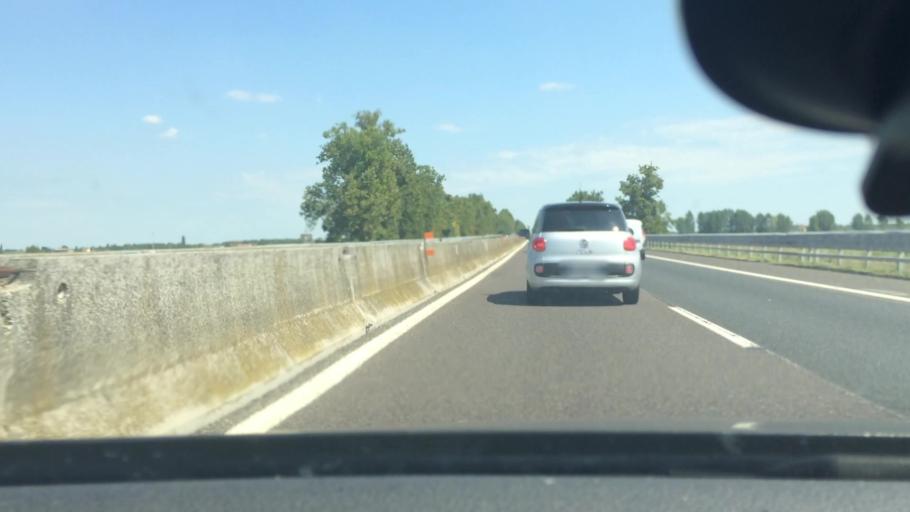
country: IT
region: Emilia-Romagna
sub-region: Provincia di Bologna
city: Malalbergo
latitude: 44.7198
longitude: 11.5056
